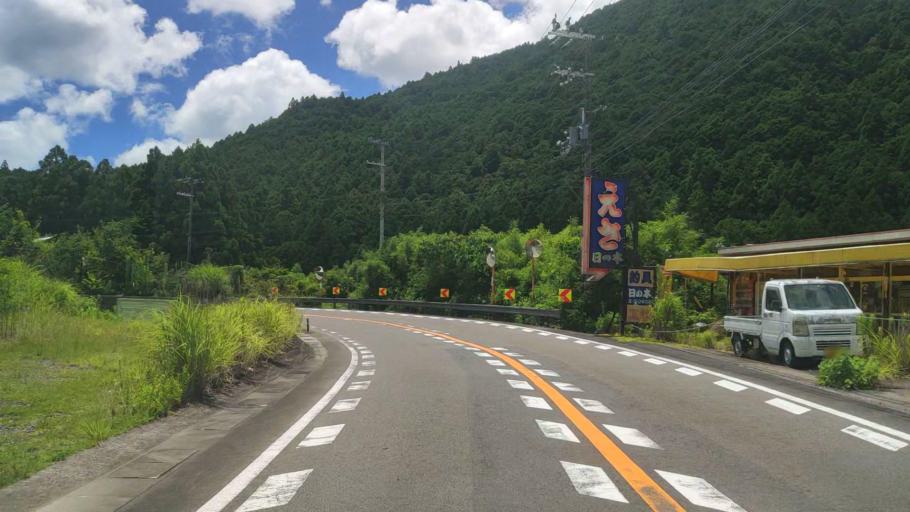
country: JP
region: Mie
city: Owase
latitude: 33.9636
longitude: 136.0608
